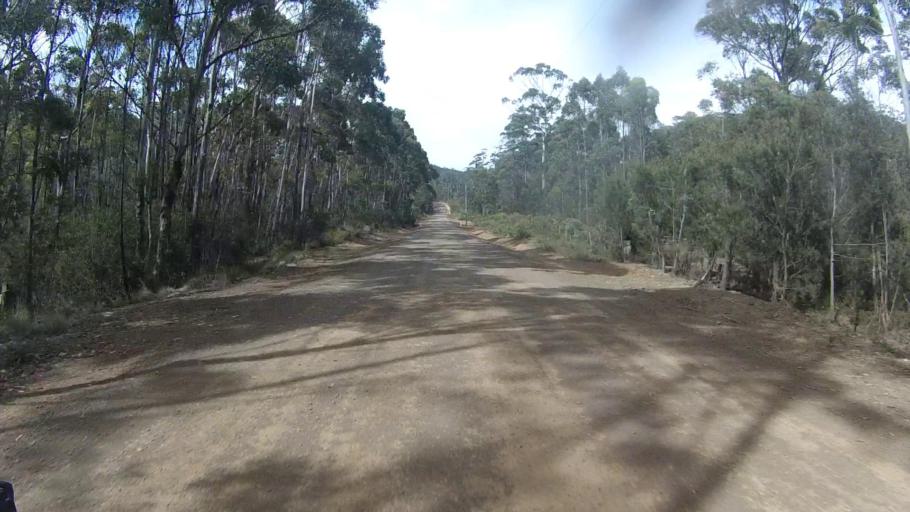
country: AU
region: Tasmania
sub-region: Sorell
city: Sorell
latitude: -42.6792
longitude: 147.8826
